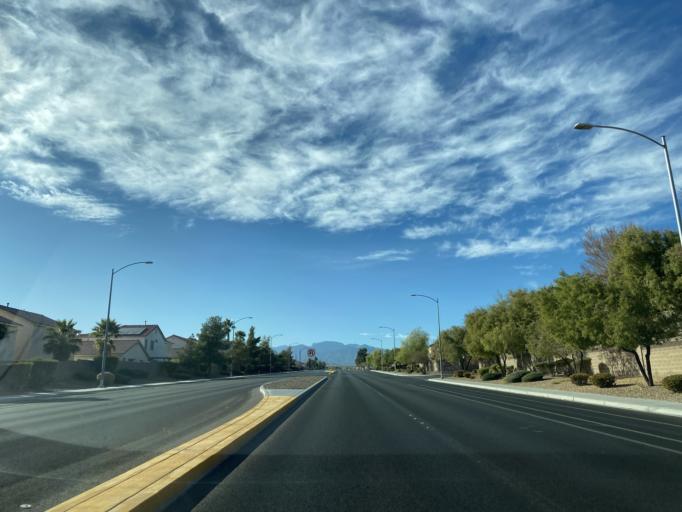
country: US
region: Nevada
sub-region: Clark County
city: Summerlin South
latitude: 36.3066
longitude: -115.2843
